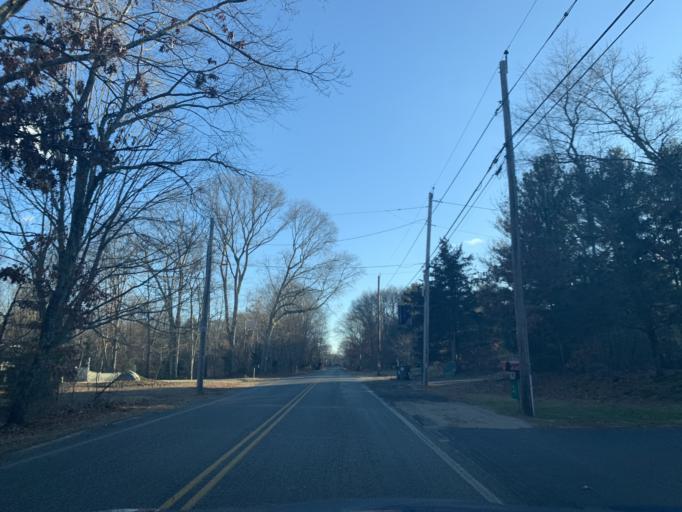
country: US
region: Massachusetts
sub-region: Bristol County
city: Norton
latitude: 41.9077
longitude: -71.2028
